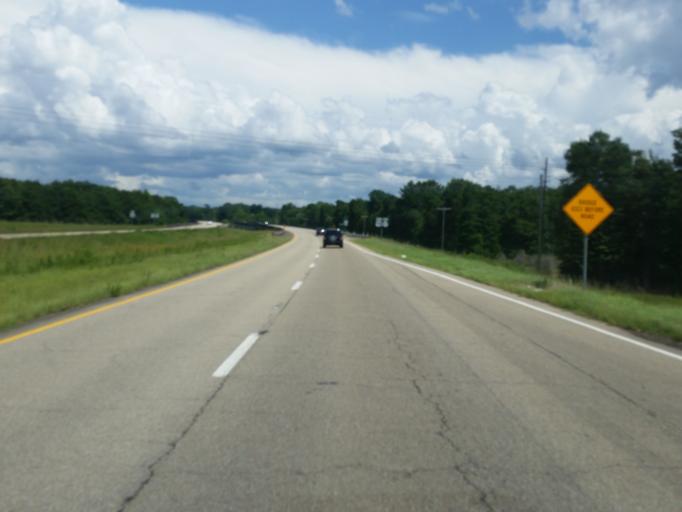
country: US
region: Mississippi
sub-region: Perry County
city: New Augusta
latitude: 31.1092
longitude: -88.8138
